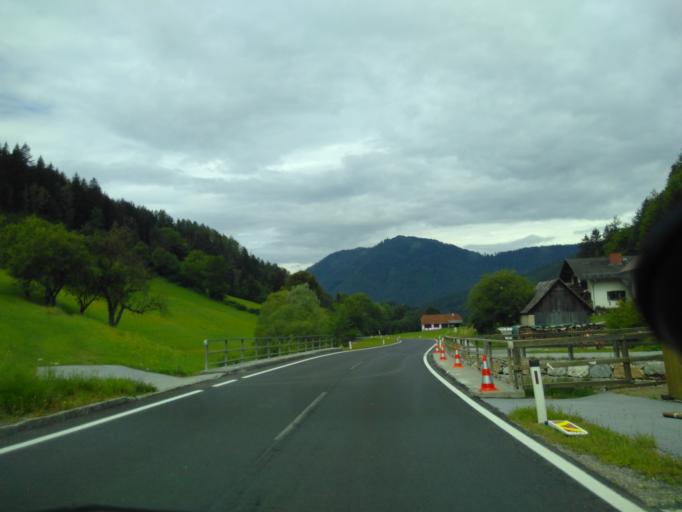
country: AT
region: Styria
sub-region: Politischer Bezirk Graz-Umgebung
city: Schrems bei Frohnleiten
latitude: 47.2738
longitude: 15.3879
